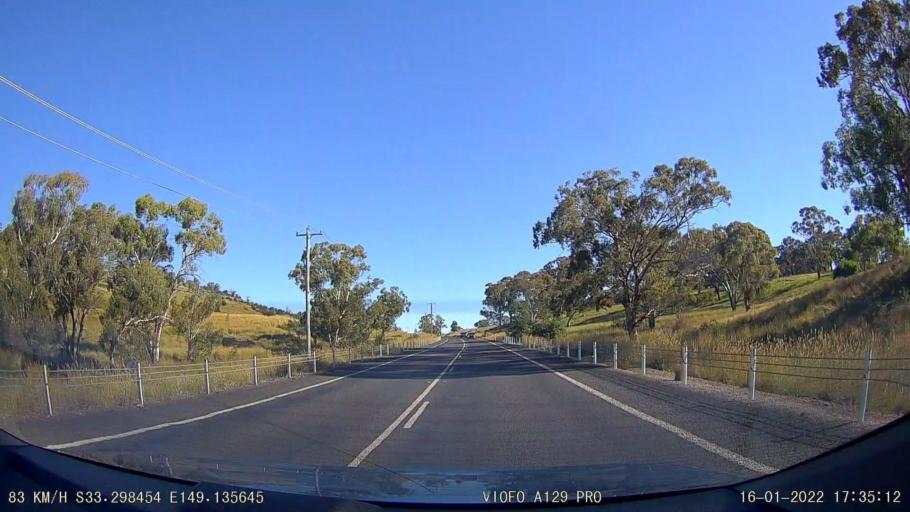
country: AU
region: New South Wales
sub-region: Orange Municipality
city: Orange
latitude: -33.2983
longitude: 149.1357
